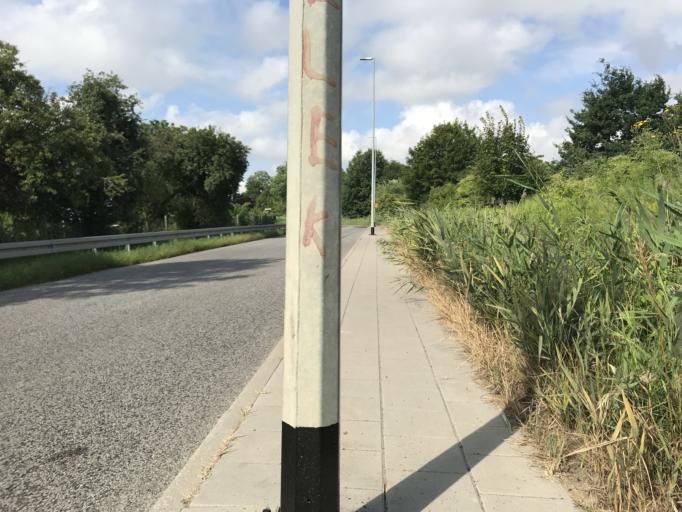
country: PL
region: Pomeranian Voivodeship
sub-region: Gdansk
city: Gdansk
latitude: 54.3403
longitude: 18.6675
